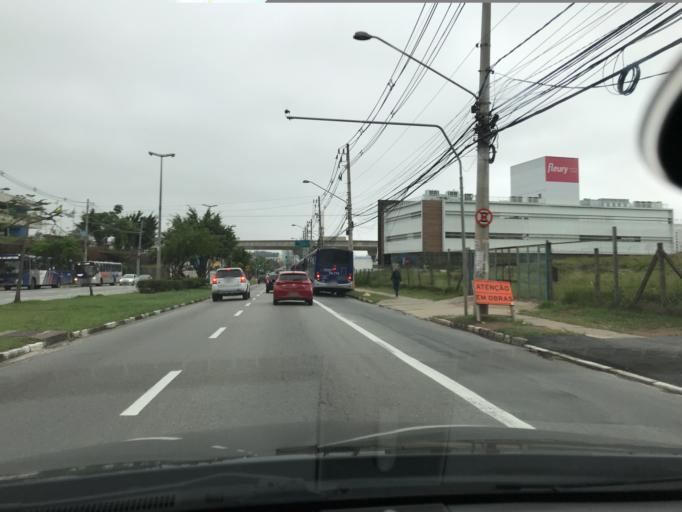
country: BR
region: Sao Paulo
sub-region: Carapicuiba
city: Carapicuiba
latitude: -23.5011
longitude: -46.8398
